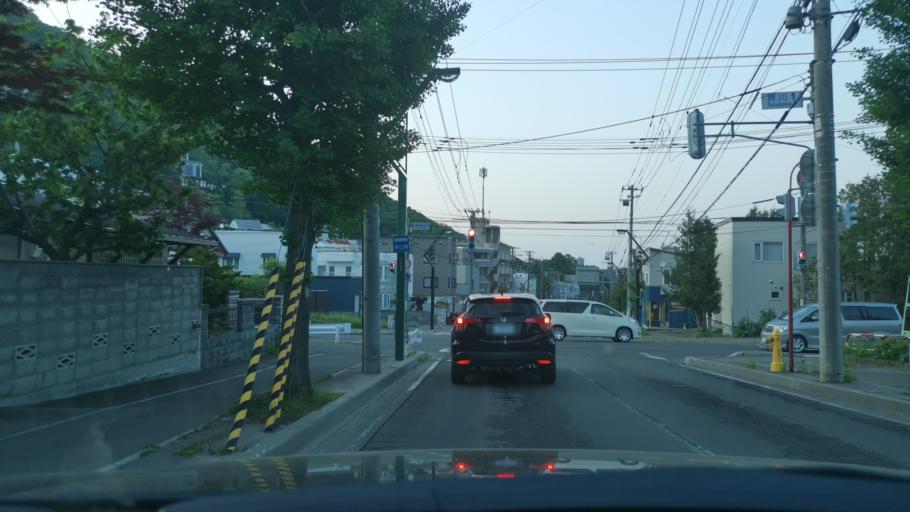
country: JP
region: Hokkaido
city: Sapporo
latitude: 43.0407
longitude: 141.3178
